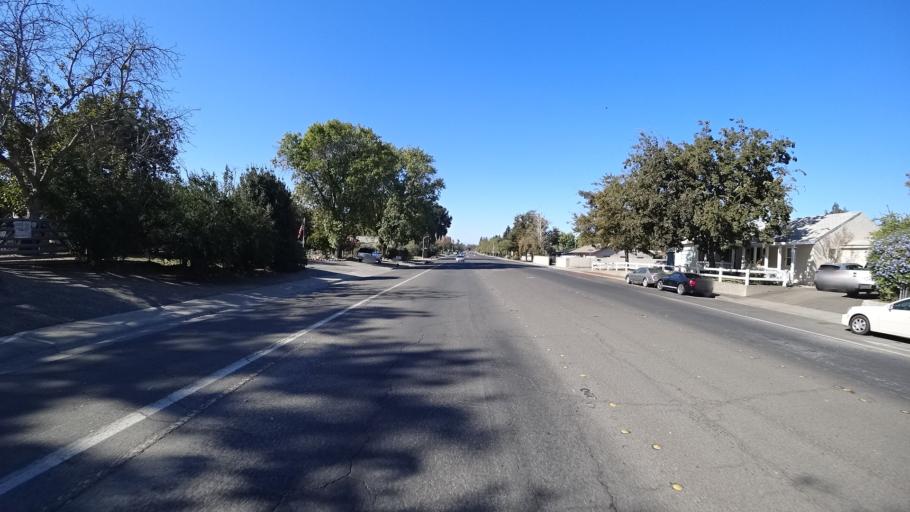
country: US
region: California
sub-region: Yolo County
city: Woodland
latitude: 38.6631
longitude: -121.7960
